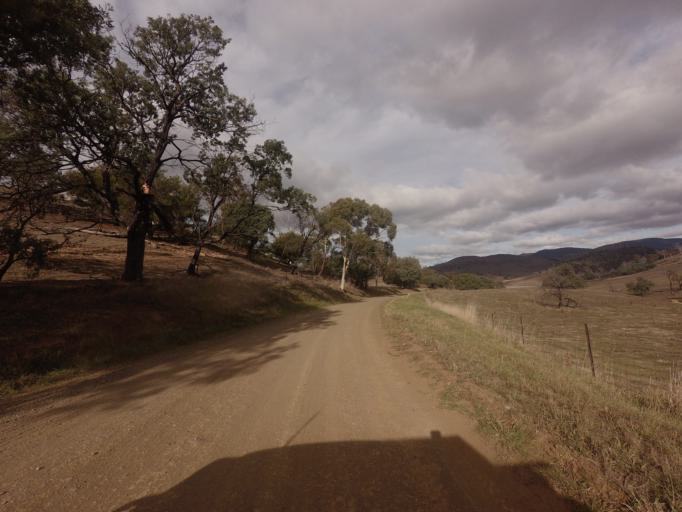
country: AU
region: Tasmania
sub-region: Brighton
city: Bridgewater
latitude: -42.4591
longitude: 147.2703
